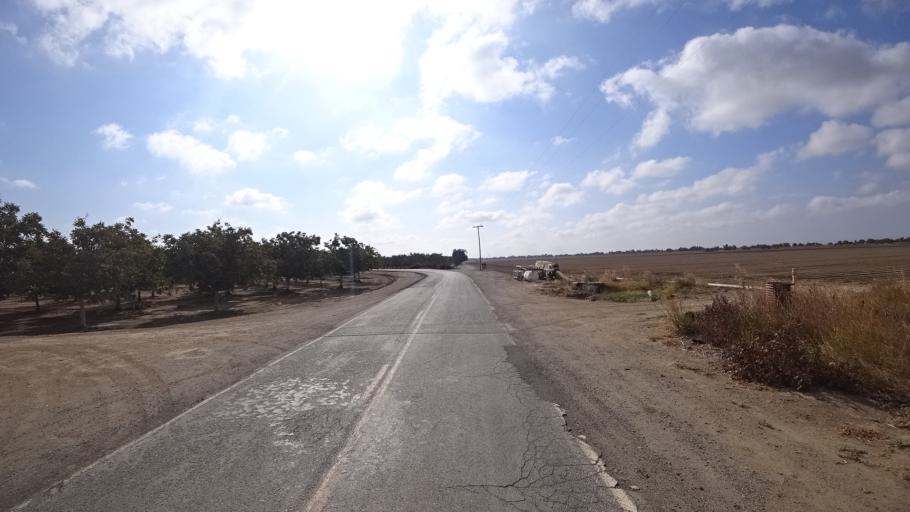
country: US
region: California
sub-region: Yolo County
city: Woodland
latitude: 38.7921
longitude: -121.7004
